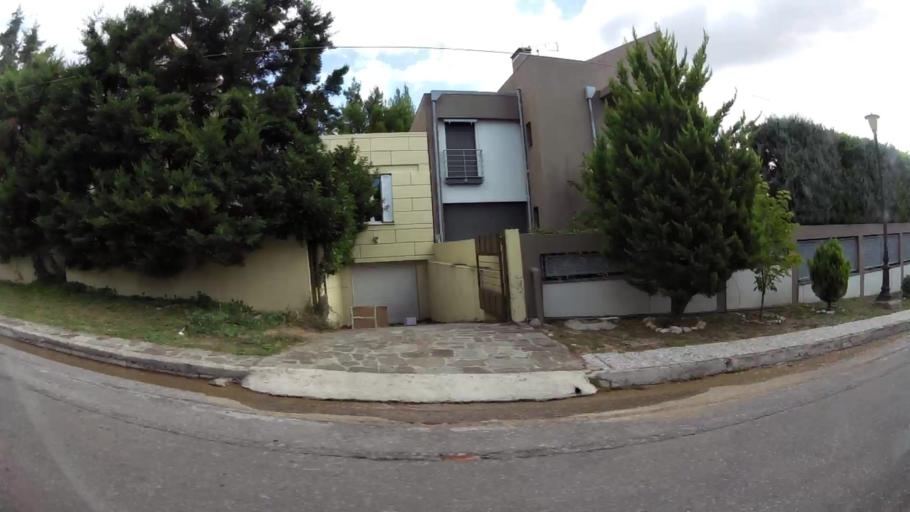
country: GR
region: Attica
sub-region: Nomarchia Anatolikis Attikis
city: Thrakomakedones
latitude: 38.1285
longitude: 23.7582
